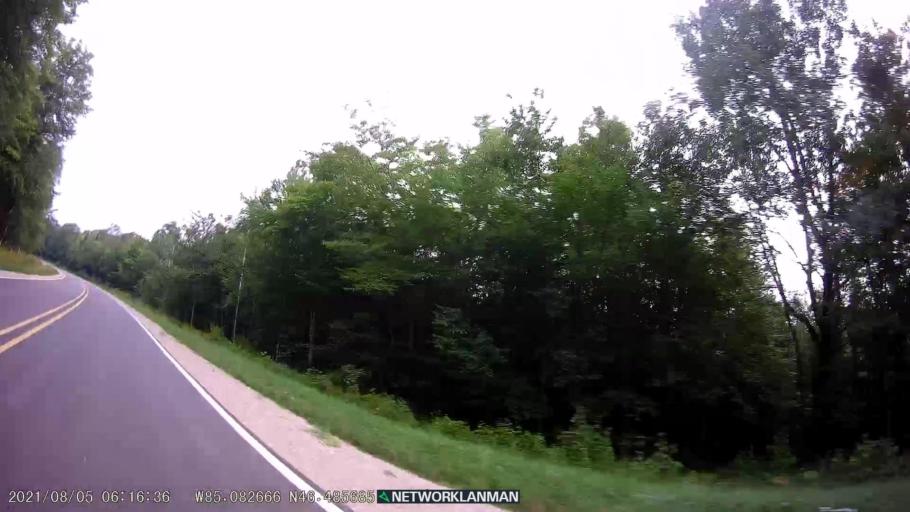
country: US
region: Michigan
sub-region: Luce County
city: Newberry
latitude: 46.4868
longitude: -85.0848
